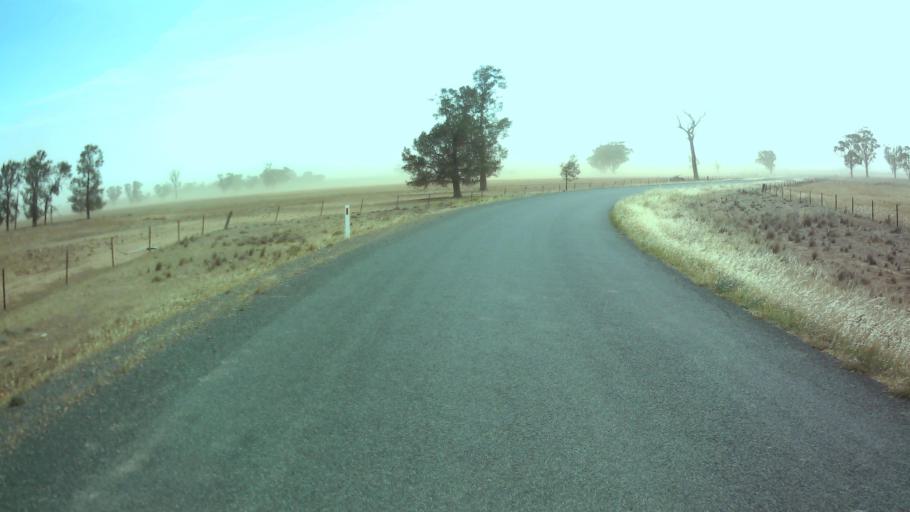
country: AU
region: New South Wales
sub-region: Weddin
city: Grenfell
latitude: -33.7375
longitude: 147.9936
